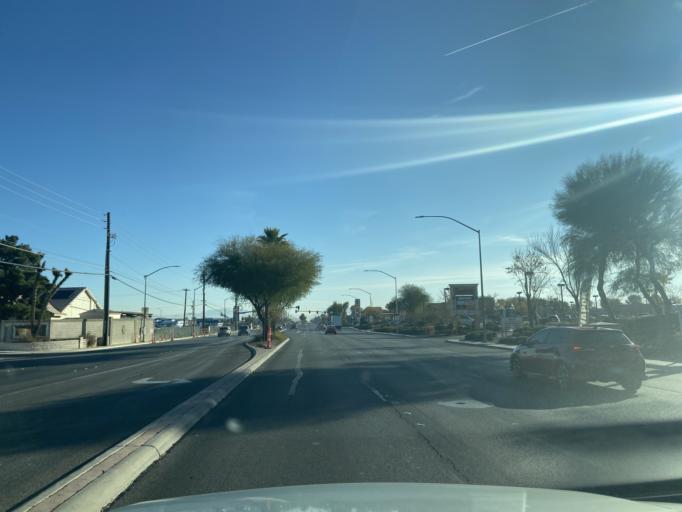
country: US
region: Nevada
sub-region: Clark County
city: North Las Vegas
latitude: 36.2394
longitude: -115.1825
